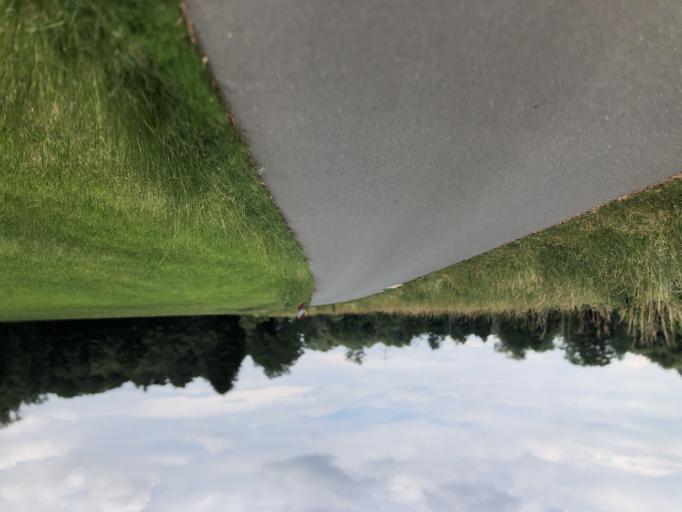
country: DE
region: Bavaria
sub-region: Regierungsbezirk Mittelfranken
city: Obermichelbach
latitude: 49.5604
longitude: 10.9259
